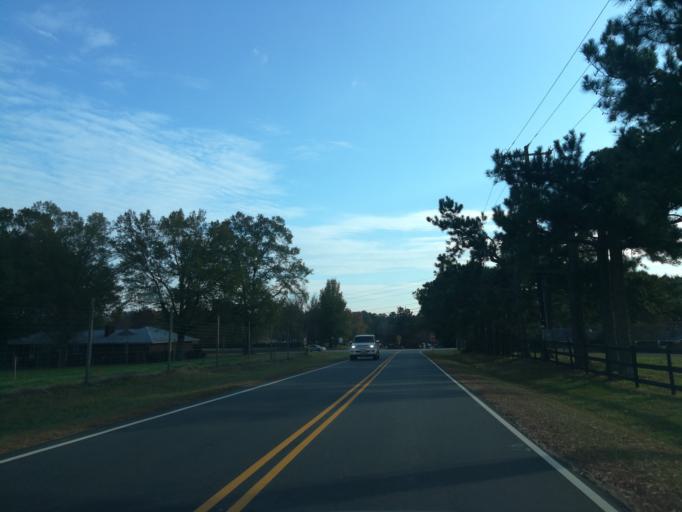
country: US
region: North Carolina
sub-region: Durham County
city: Durham
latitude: 35.9911
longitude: -78.9940
